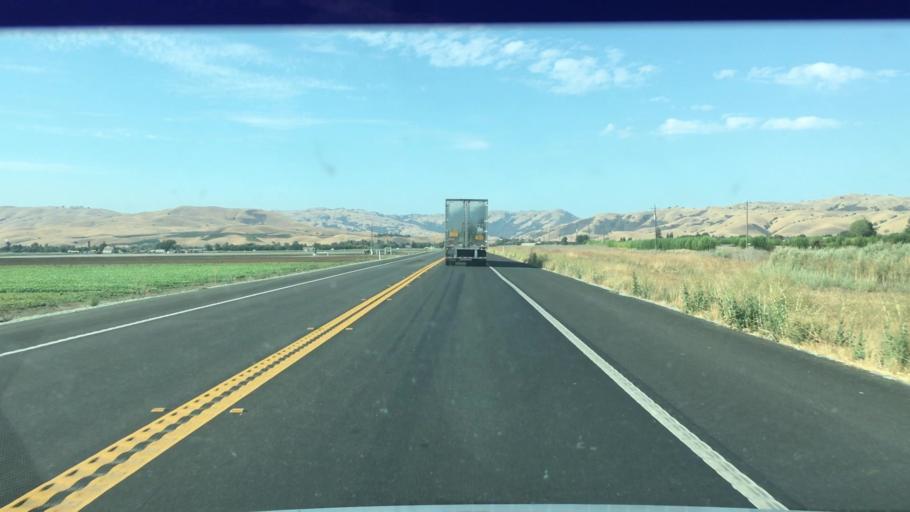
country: US
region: California
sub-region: San Benito County
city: Hollister
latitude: 36.9199
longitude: -121.3918
